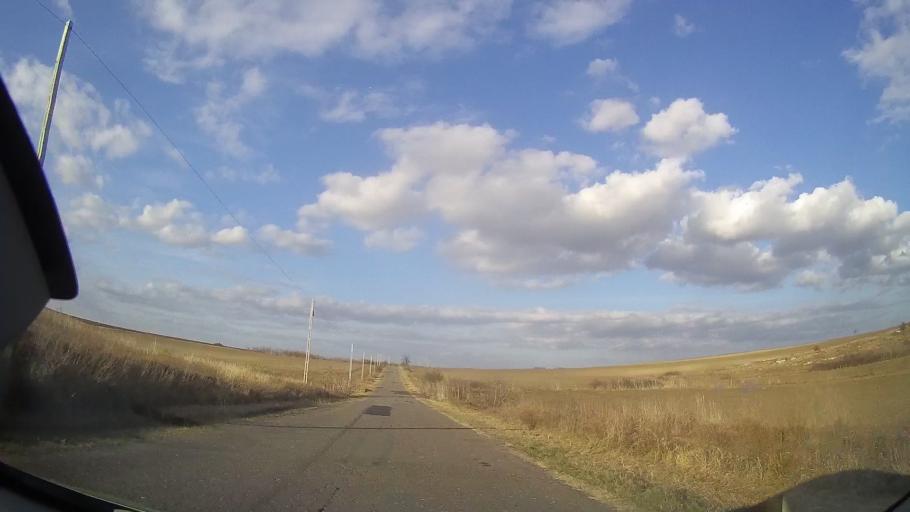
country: RO
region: Constanta
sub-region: Comuna Cerchezu
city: Cerchezu
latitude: 43.8427
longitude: 28.0984
